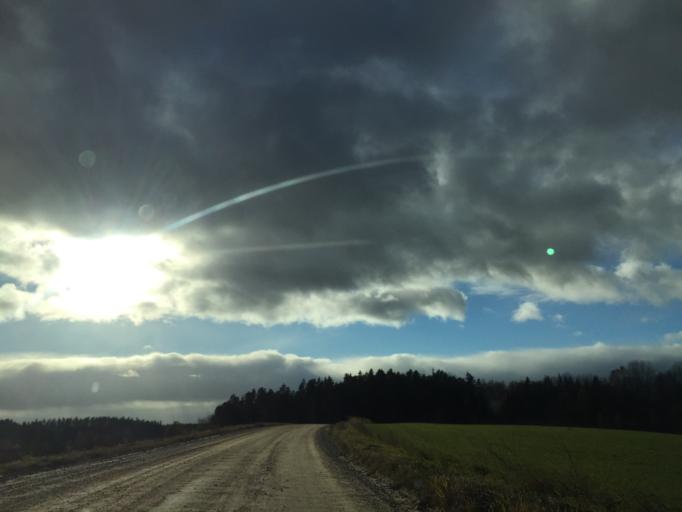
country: LV
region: Tukuma Rajons
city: Tukums
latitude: 56.9815
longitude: 23.0255
